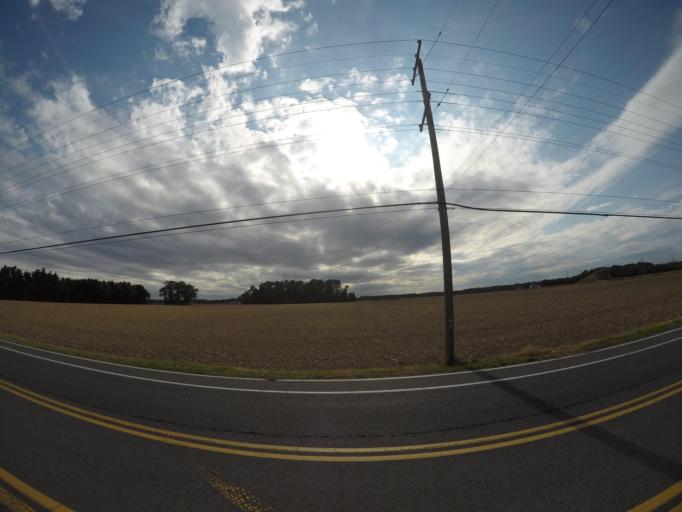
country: US
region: Delaware
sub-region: Sussex County
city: Lewes
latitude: 38.7298
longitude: -75.1492
